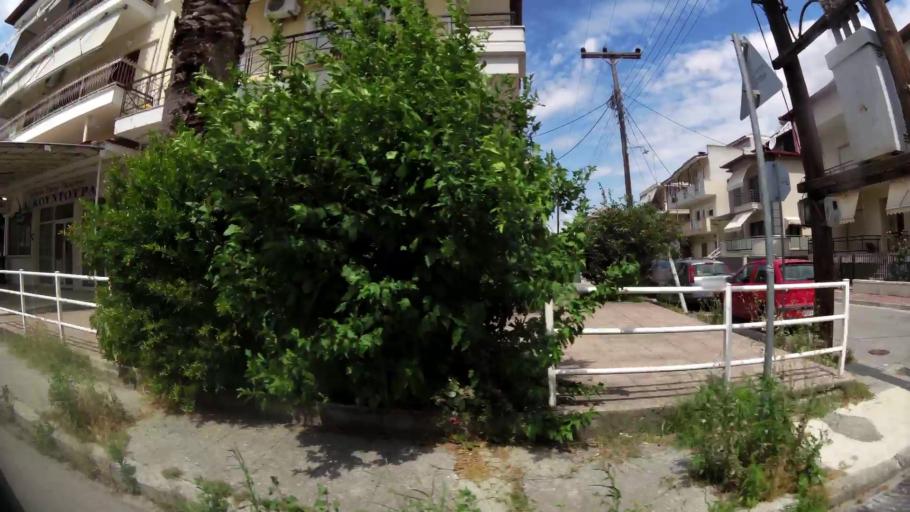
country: GR
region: Central Macedonia
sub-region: Nomos Pierias
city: Katerini
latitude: 40.2746
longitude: 22.4990
